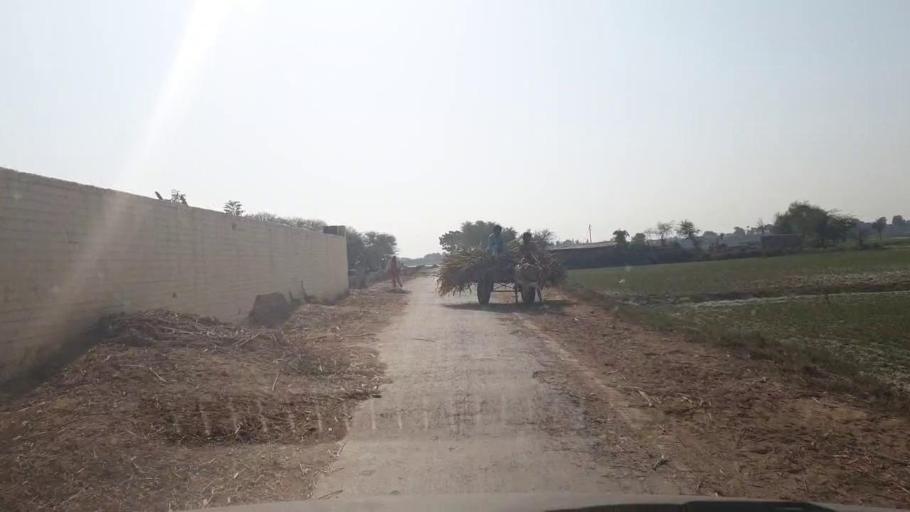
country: PK
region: Sindh
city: Tando Adam
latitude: 25.7446
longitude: 68.6166
